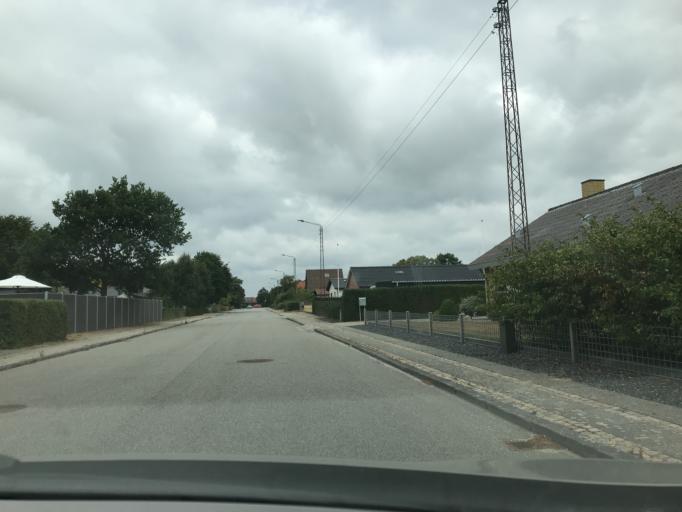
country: DK
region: Central Jutland
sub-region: Ringkobing-Skjern Kommune
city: Tarm
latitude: 55.9016
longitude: 8.5126
